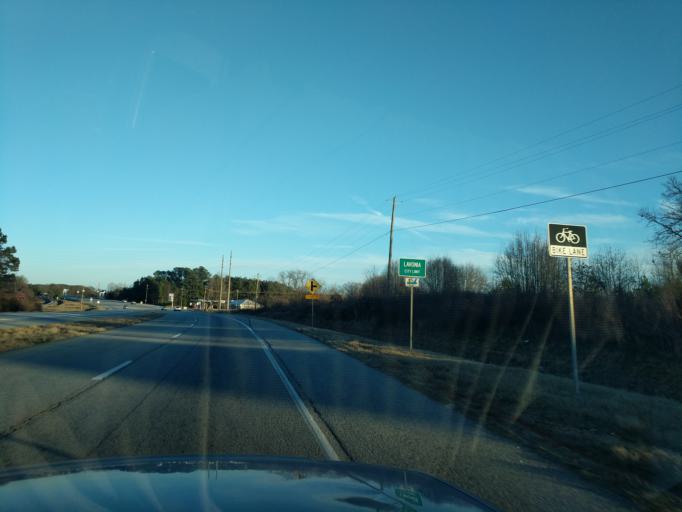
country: US
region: Georgia
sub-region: Franklin County
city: Lavonia
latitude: 34.4478
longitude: -83.1420
